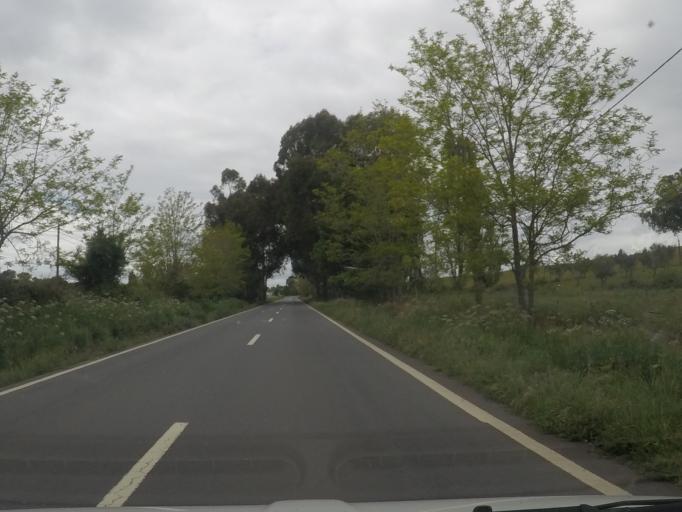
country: PT
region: Setubal
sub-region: Santiago do Cacem
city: Cercal
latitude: 37.8225
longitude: -8.6887
